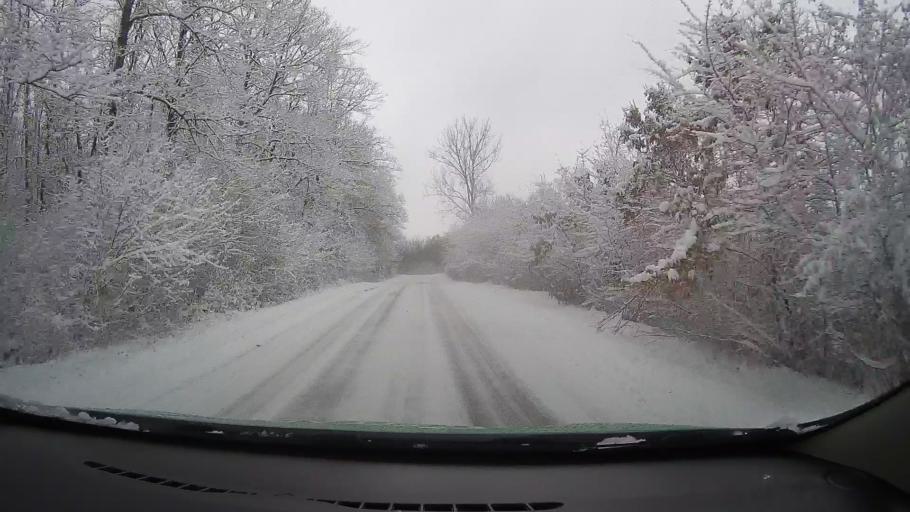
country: RO
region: Hunedoara
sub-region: Comuna Pestisu Mic
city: Pestisu Mic
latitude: 45.8134
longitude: 22.8986
